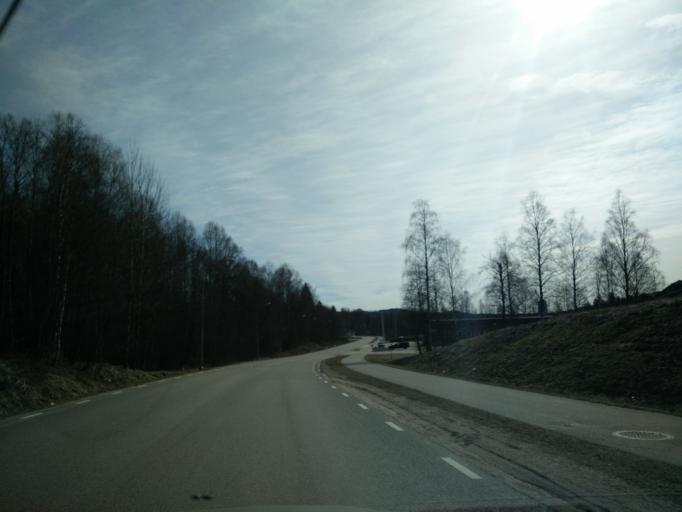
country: SE
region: Vaermland
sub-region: Hagfors Kommun
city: Hagfors
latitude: 60.0246
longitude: 13.6929
